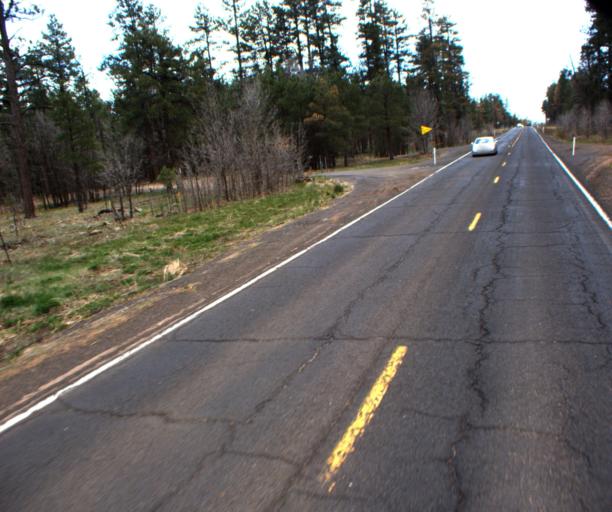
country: US
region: Arizona
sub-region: Coconino County
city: Kachina Village
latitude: 35.0893
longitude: -111.7311
